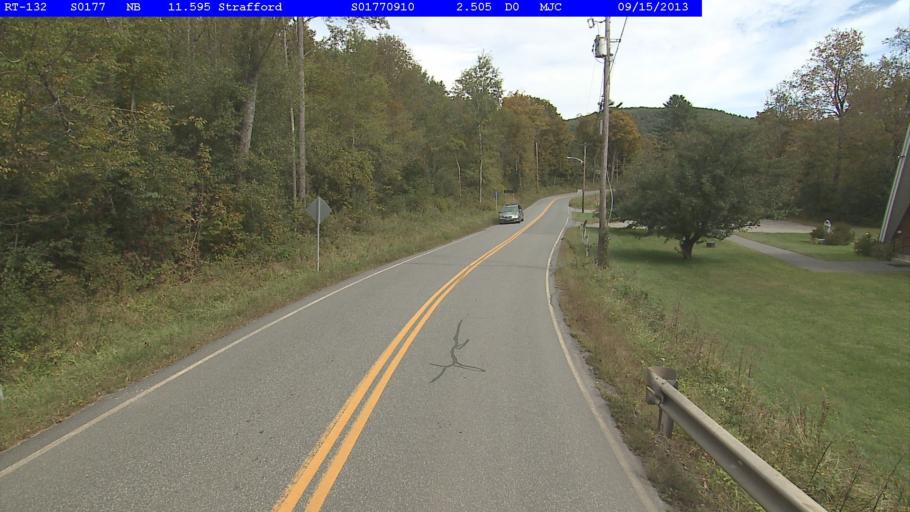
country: US
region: New Hampshire
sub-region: Grafton County
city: Hanover
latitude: 43.8347
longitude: -72.3596
